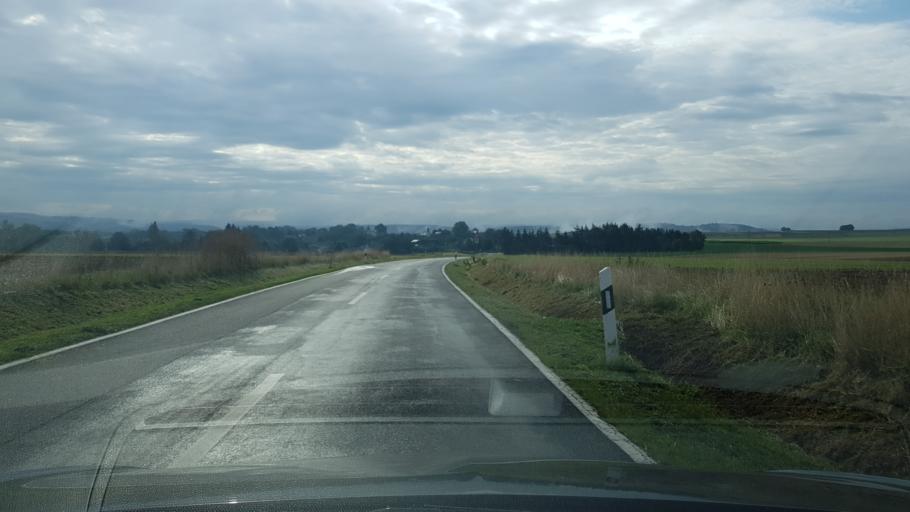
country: DE
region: Rheinland-Pfalz
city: Munstermaifeld
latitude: 50.2428
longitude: 7.3724
